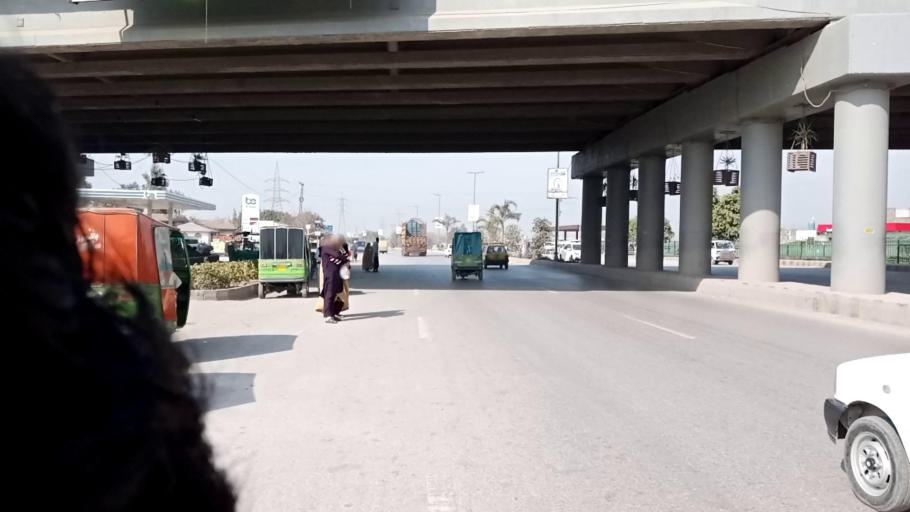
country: PK
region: Khyber Pakhtunkhwa
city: Peshawar
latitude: 34.0236
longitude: 71.6206
